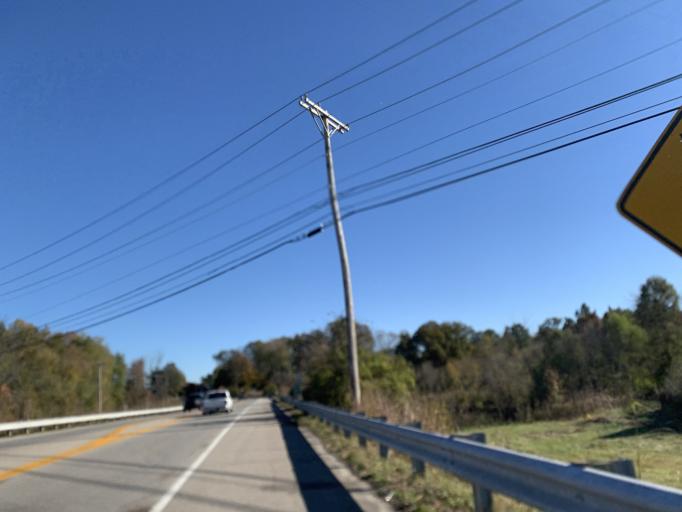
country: US
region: Kentucky
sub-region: Jefferson County
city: Pleasure Ridge Park
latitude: 38.1463
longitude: -85.8848
